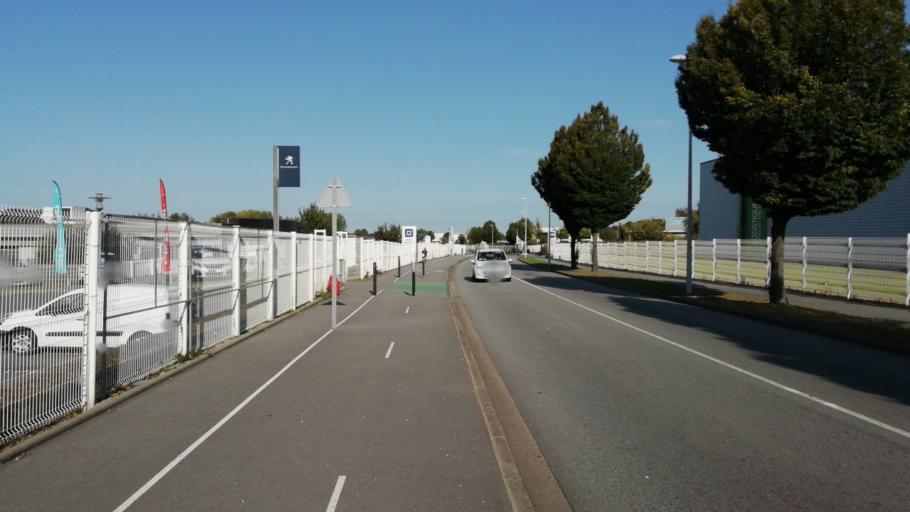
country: FR
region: Haute-Normandie
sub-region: Departement de la Seine-Maritime
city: Harfleur
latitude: 49.5074
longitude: 0.2168
